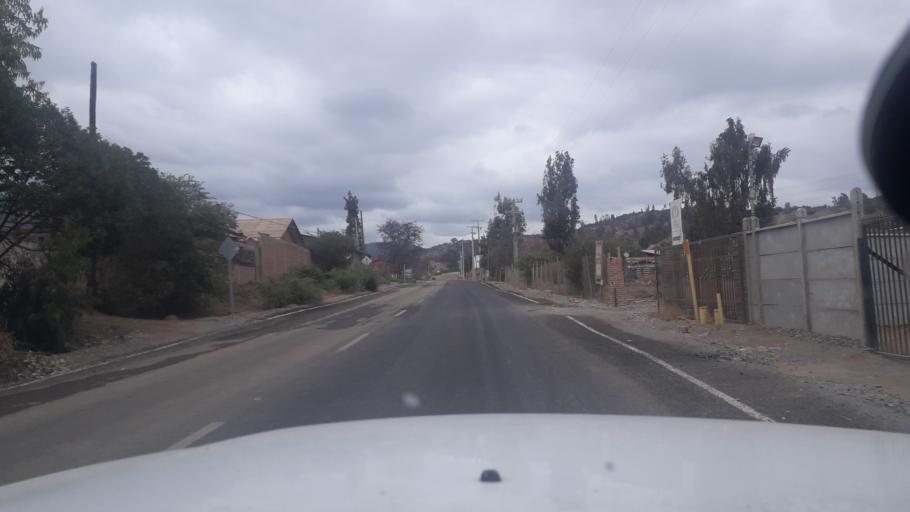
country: CL
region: Valparaiso
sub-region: Provincia de Marga Marga
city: Limache
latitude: -33.0289
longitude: -71.2759
